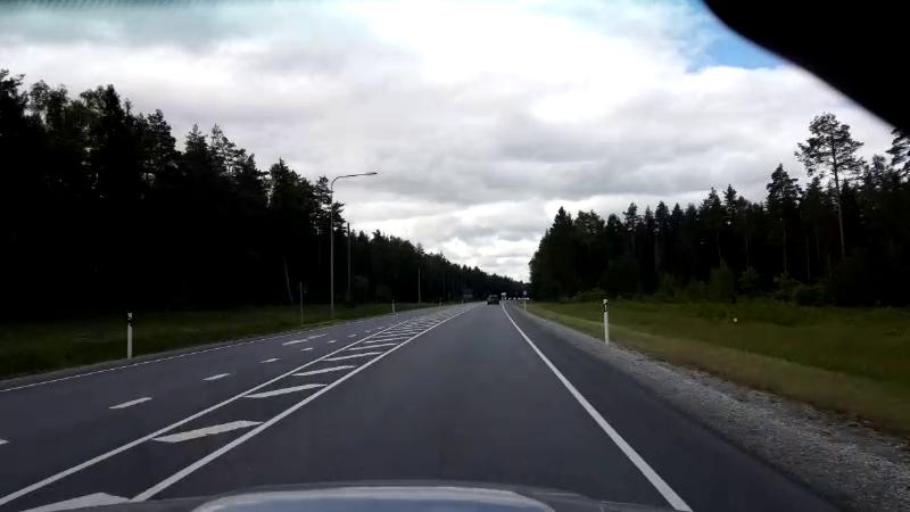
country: EE
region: Raplamaa
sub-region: Maerjamaa vald
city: Marjamaa
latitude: 58.8937
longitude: 24.4549
